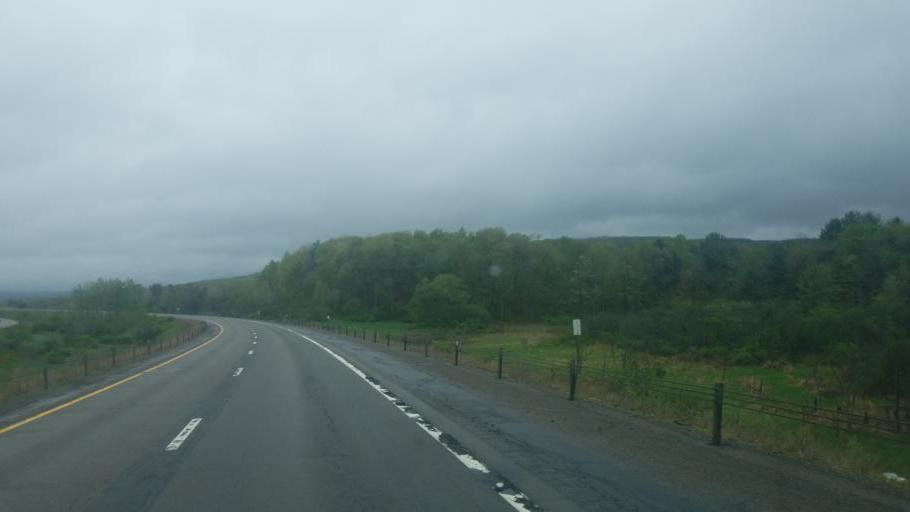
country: US
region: New York
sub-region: Allegany County
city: Belmont
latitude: 42.3010
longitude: -77.9466
